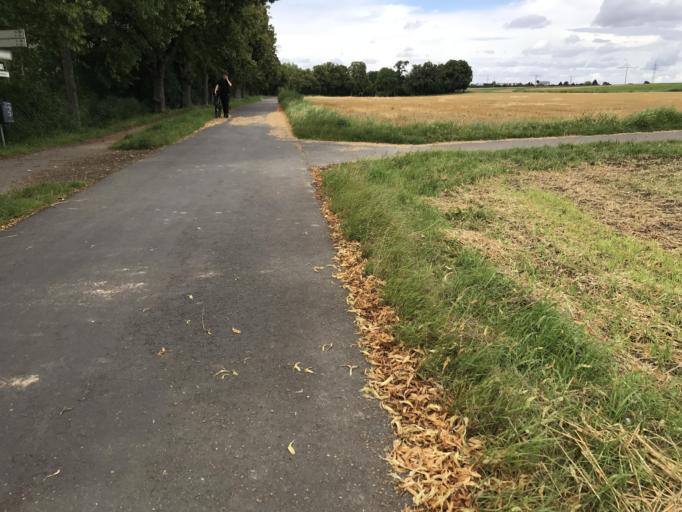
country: DE
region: Hesse
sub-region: Regierungsbezirk Darmstadt
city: Friedberg
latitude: 50.3369
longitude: 8.7698
